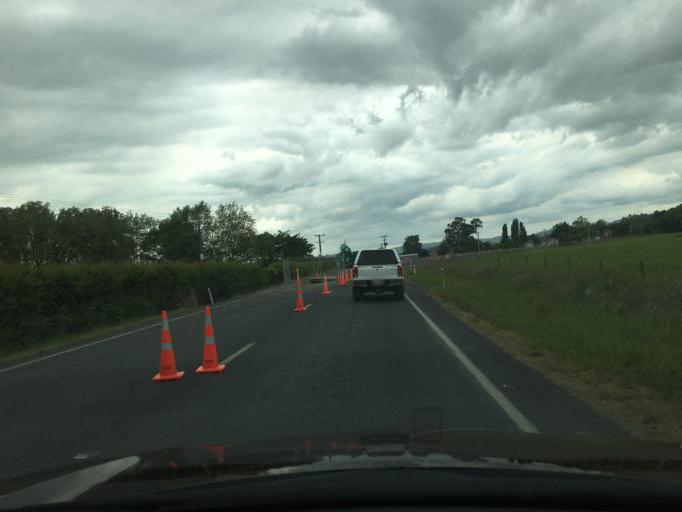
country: NZ
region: Waikato
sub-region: Waipa District
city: Cambridge
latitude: -37.9201
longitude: 175.4375
